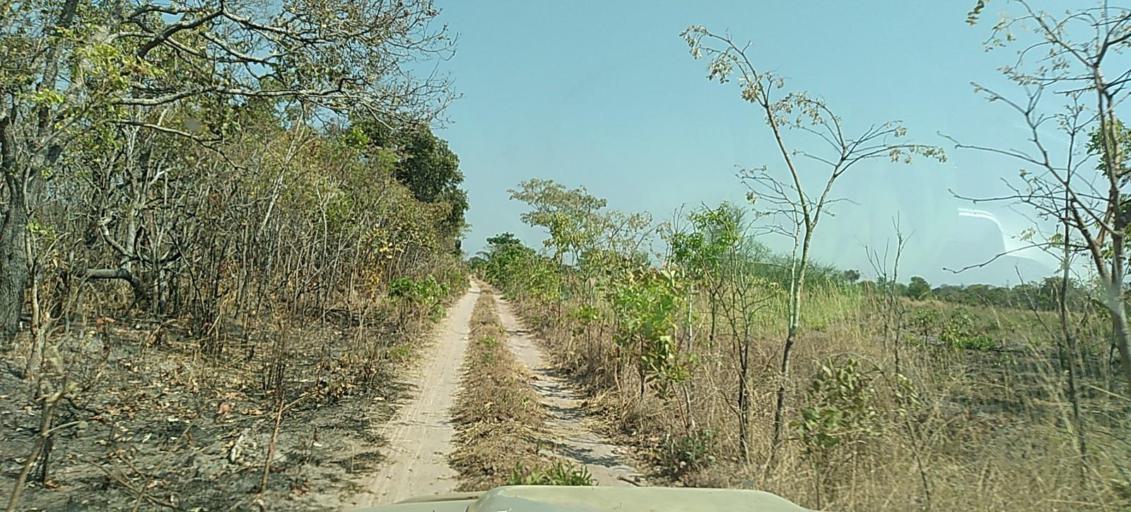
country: ZM
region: North-Western
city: Kalengwa
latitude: -13.3196
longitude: 24.8204
